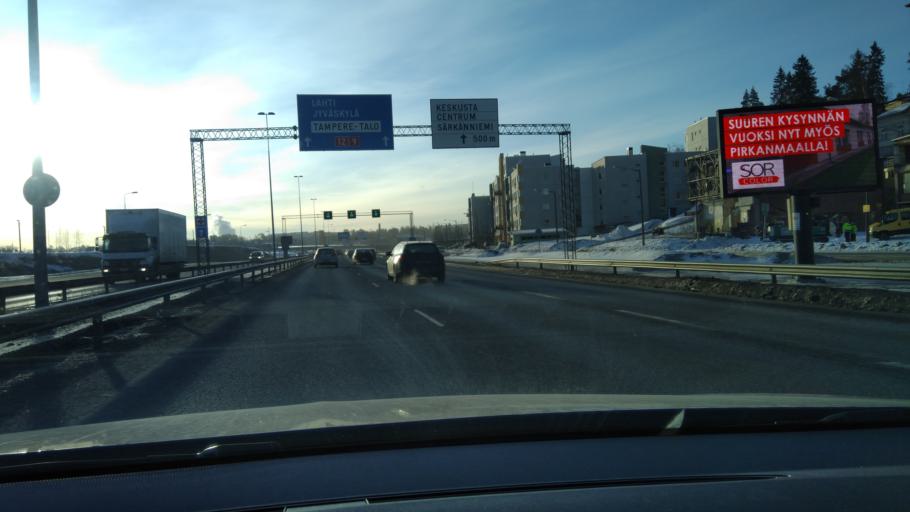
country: FI
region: Pirkanmaa
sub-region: Tampere
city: Tampere
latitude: 61.5058
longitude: 23.7157
